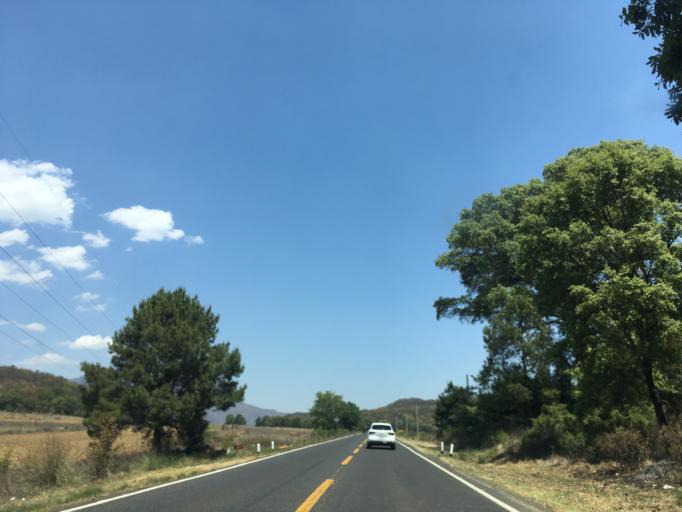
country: MX
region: Michoacan
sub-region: Chilchota
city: Tacuro (Santa Maria Tacuro)
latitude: 19.8153
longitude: -102.0286
